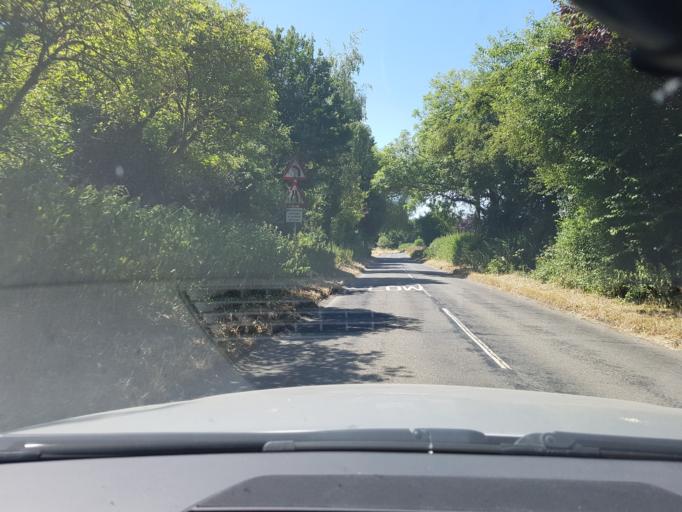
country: GB
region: England
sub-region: Northamptonshire
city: Deanshanger
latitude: 52.0287
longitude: -0.8730
